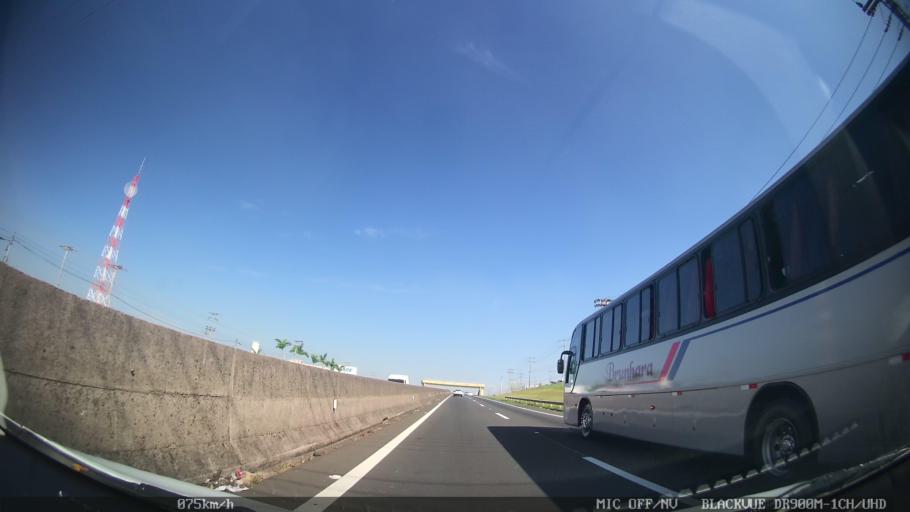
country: BR
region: Sao Paulo
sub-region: Campinas
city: Campinas
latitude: -22.9789
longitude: -47.1039
